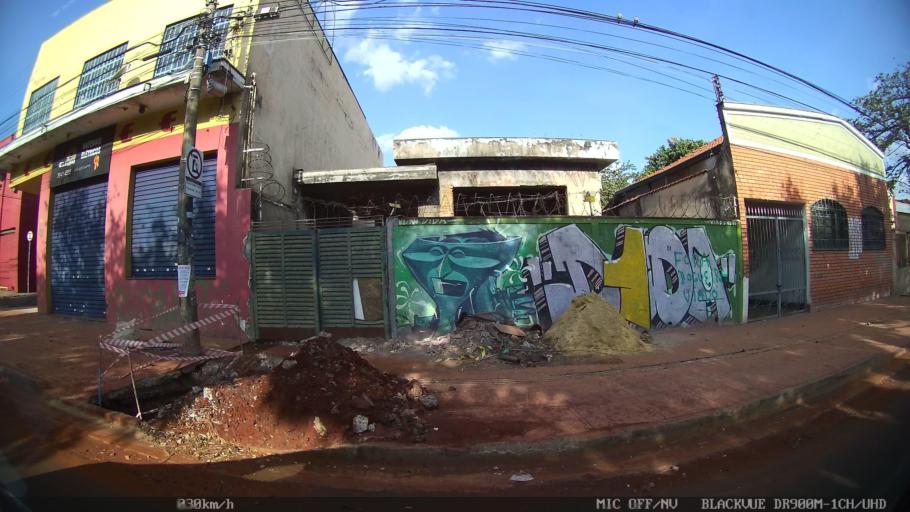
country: BR
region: Sao Paulo
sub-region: Ribeirao Preto
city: Ribeirao Preto
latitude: -21.1635
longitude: -47.8114
